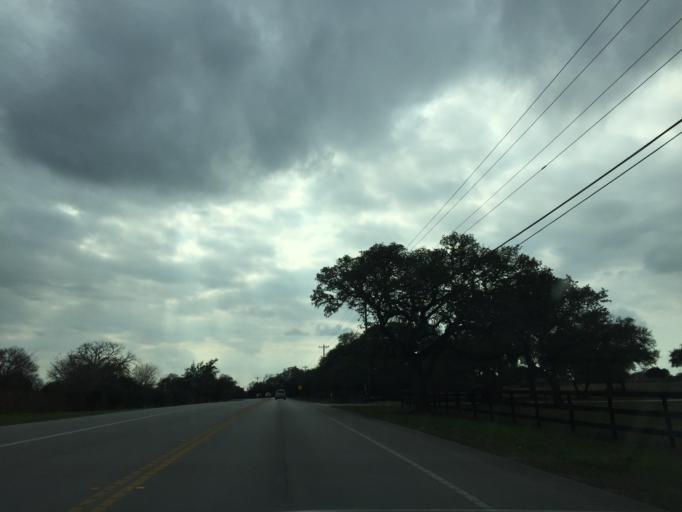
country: US
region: Texas
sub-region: Hays County
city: Dripping Springs
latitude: 30.1464
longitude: -97.9872
